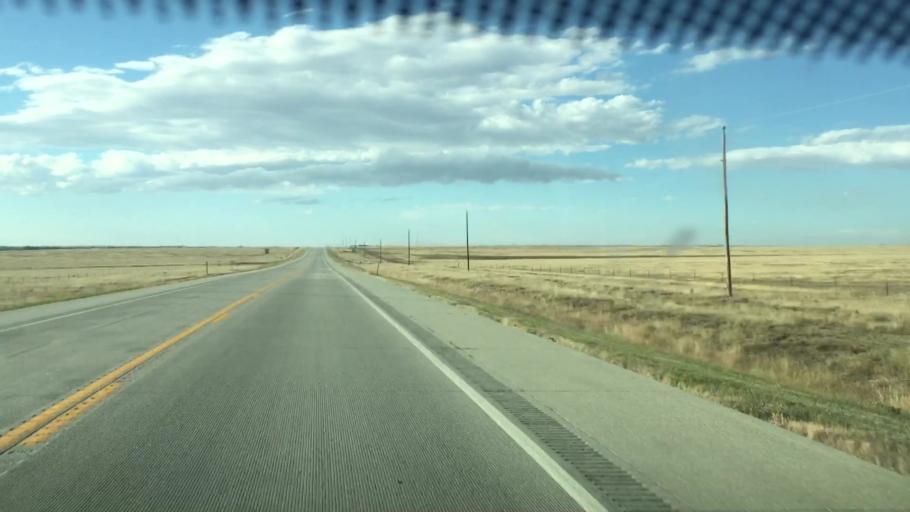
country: US
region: Colorado
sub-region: Lincoln County
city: Hugo
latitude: 39.0964
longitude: -103.4075
